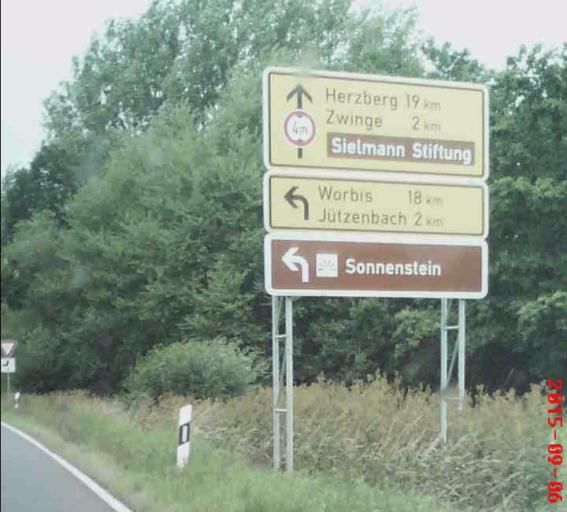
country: DE
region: Thuringia
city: Weissenborn-Luderode
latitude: 51.5390
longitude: 10.3966
